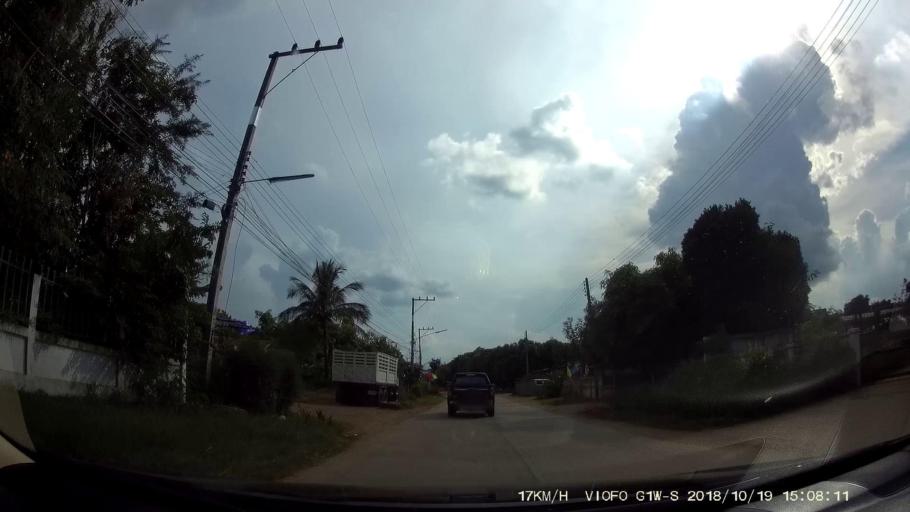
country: TH
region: Chaiyaphum
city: Phu Khiao
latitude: 16.4149
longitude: 102.1041
